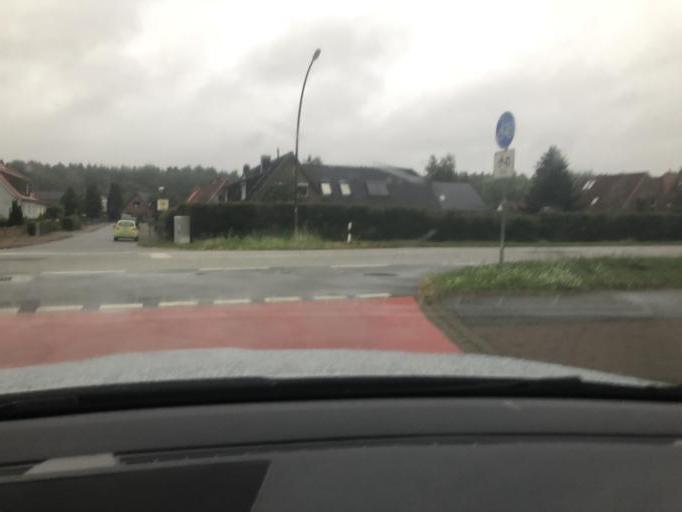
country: DE
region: Schleswig-Holstein
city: Gross Gronau
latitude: 53.8154
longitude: 10.7368
